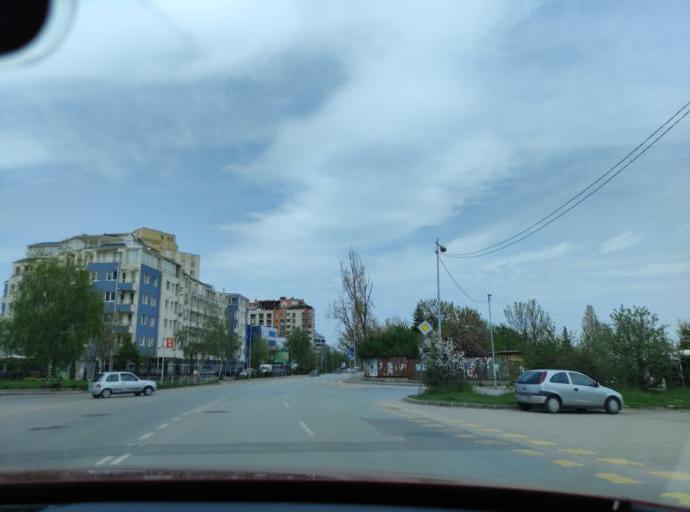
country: BG
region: Sofia-Capital
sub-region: Stolichna Obshtina
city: Sofia
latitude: 42.6466
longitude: 23.3454
